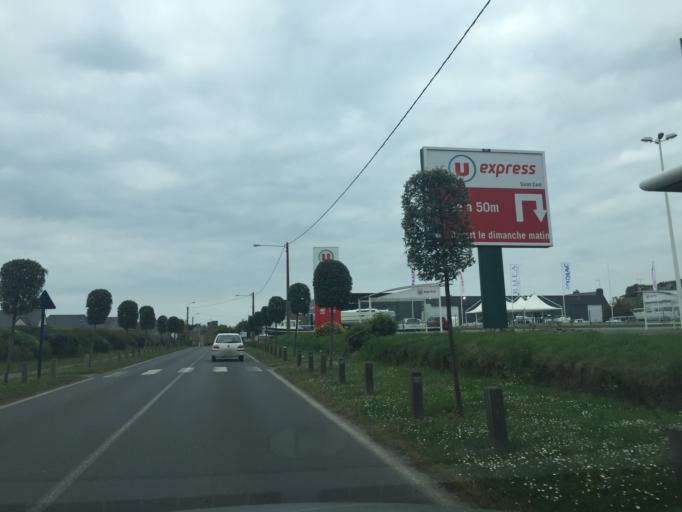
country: FR
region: Brittany
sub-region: Departement des Cotes-d'Armor
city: Saint-Cast-le-Guildo
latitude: 48.6179
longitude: -2.2664
